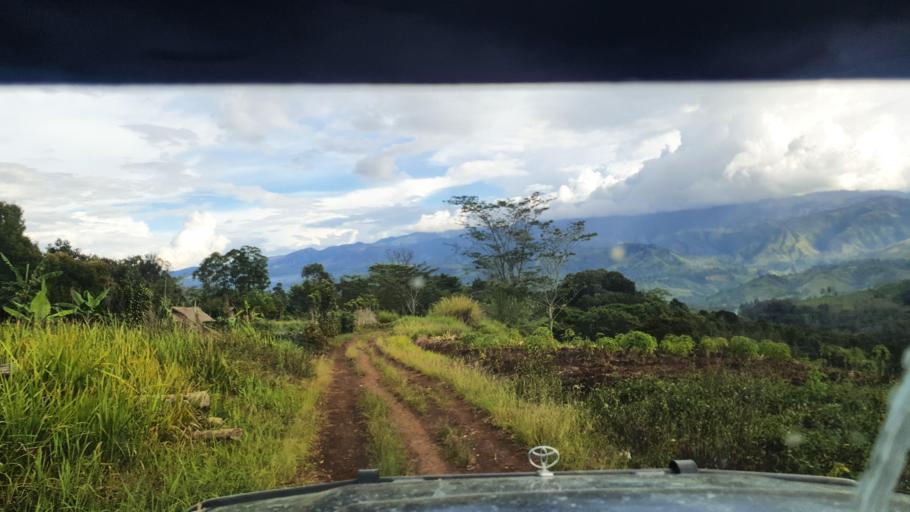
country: PG
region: Jiwaka
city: Minj
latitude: -5.9170
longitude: 144.8200
